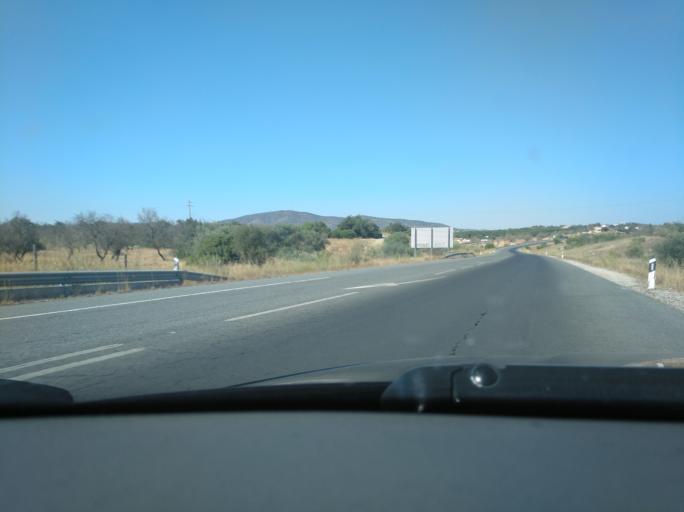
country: PT
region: Faro
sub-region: Olhao
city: Olhao
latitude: 37.0471
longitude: -7.8181
